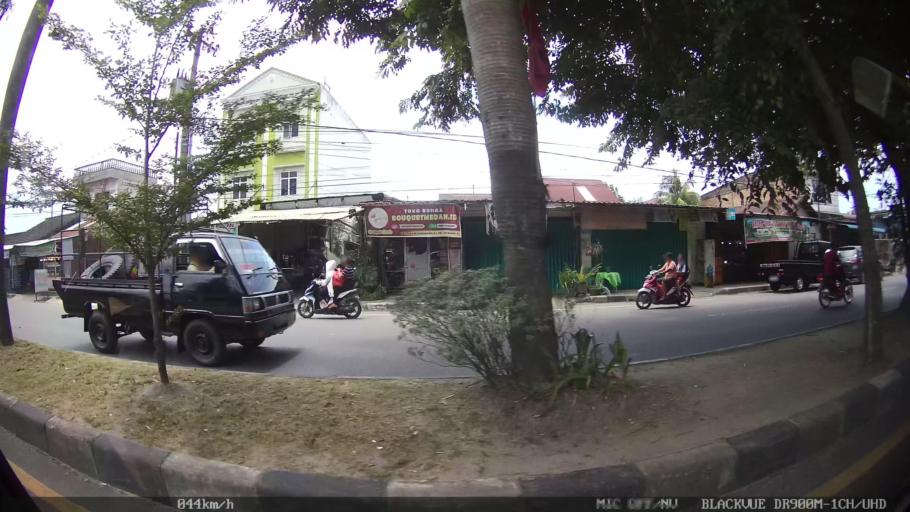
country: ID
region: North Sumatra
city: Deli Tua
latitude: 3.5322
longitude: 98.6448
